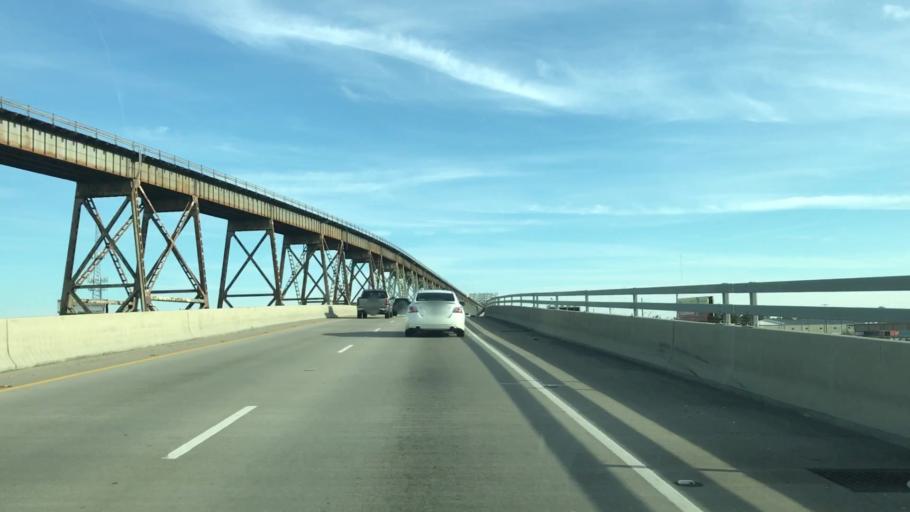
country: US
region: Louisiana
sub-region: Jefferson Parish
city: Elmwood
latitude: 29.9538
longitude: -90.1804
